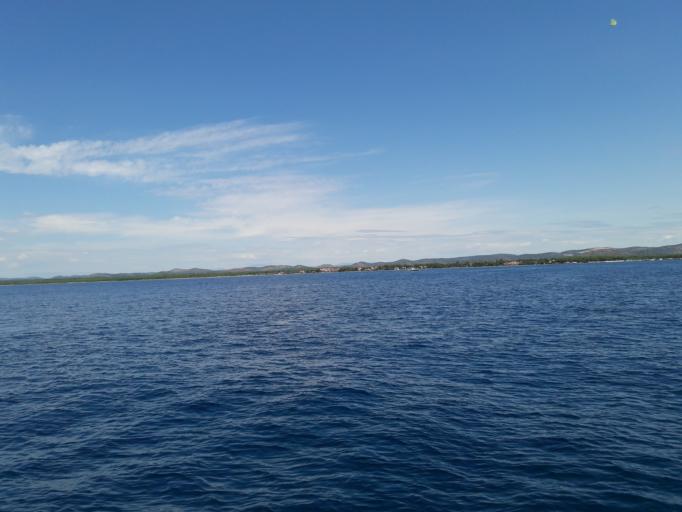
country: HR
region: Sibensko-Kniniska
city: Vodice
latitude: 43.7116
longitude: 15.8344
